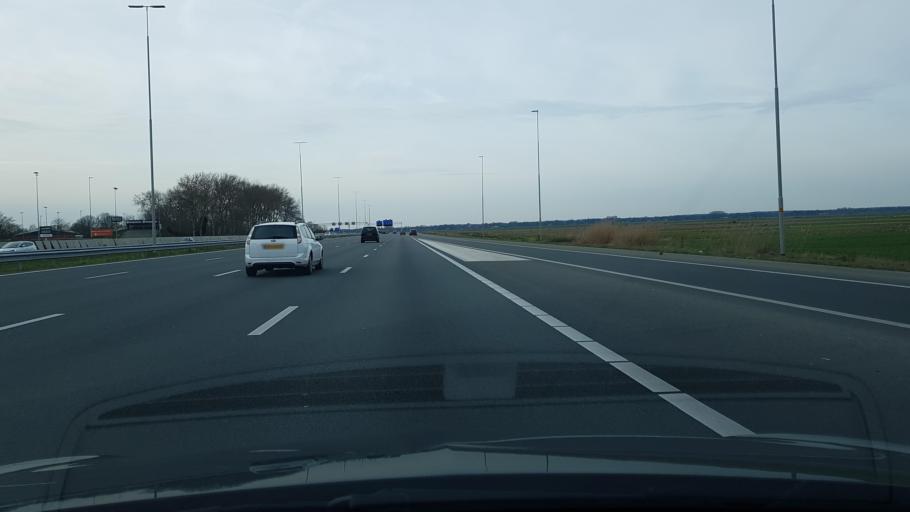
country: NL
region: Utrecht
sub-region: Gemeente Baarn
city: Baarn
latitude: 52.2207
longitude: 5.2967
